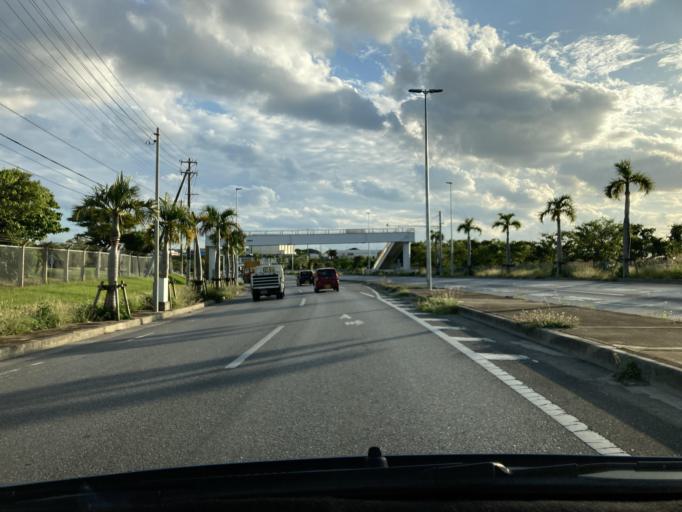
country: JP
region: Okinawa
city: Chatan
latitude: 26.3048
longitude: 127.7794
